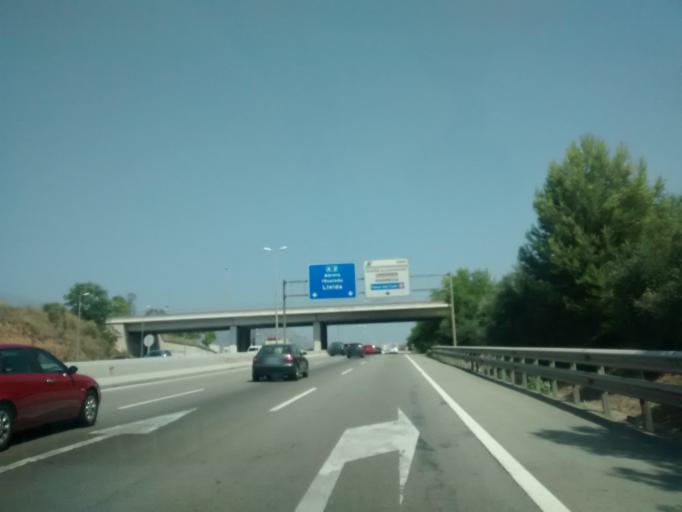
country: ES
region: Catalonia
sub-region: Provincia de Barcelona
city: Abrera
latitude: 41.5139
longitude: 1.8994
